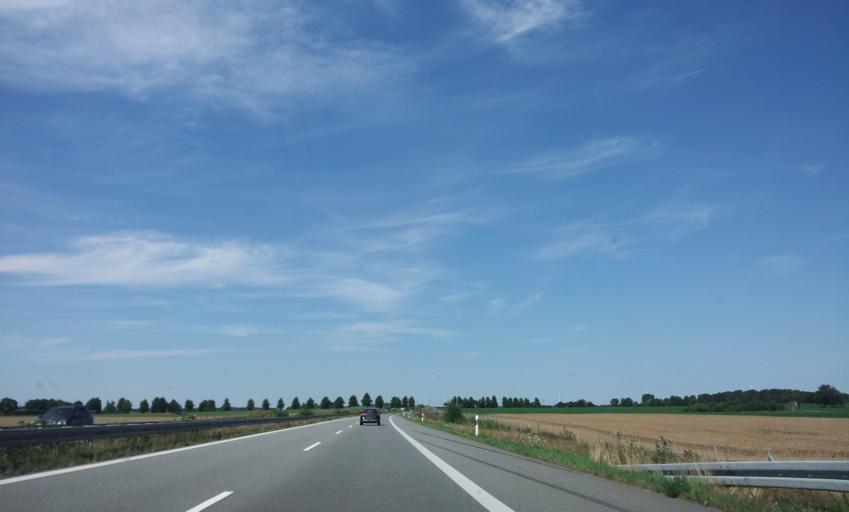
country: DE
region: Mecklenburg-Vorpommern
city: Gormin
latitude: 54.0093
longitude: 13.2954
